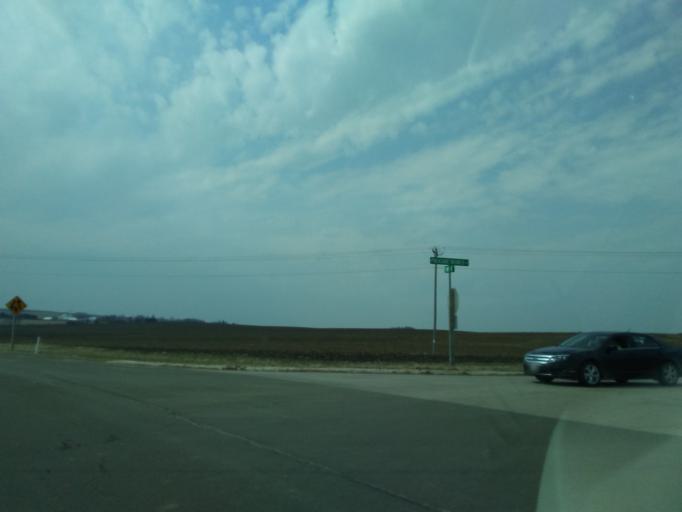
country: US
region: Wisconsin
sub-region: Dane County
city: Middleton
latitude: 43.1478
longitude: -89.4910
